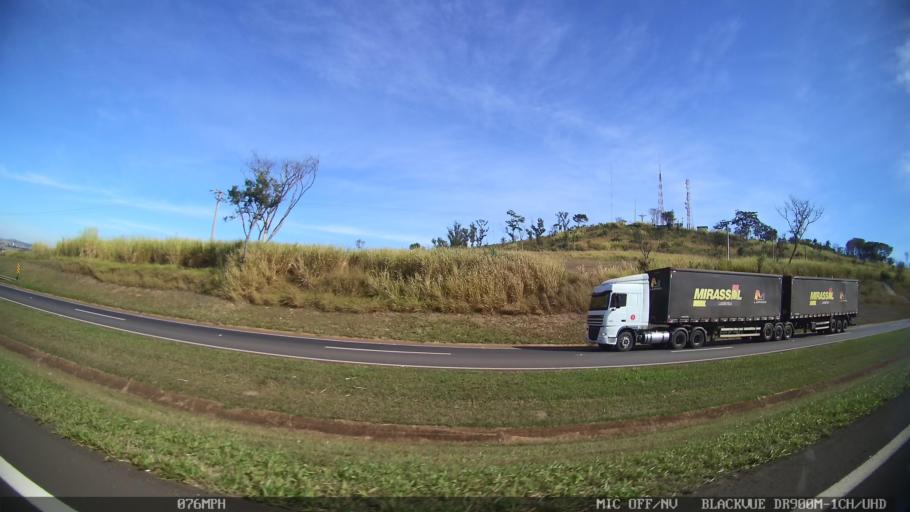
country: BR
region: Sao Paulo
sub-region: Leme
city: Leme
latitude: -22.1593
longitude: -47.3999
